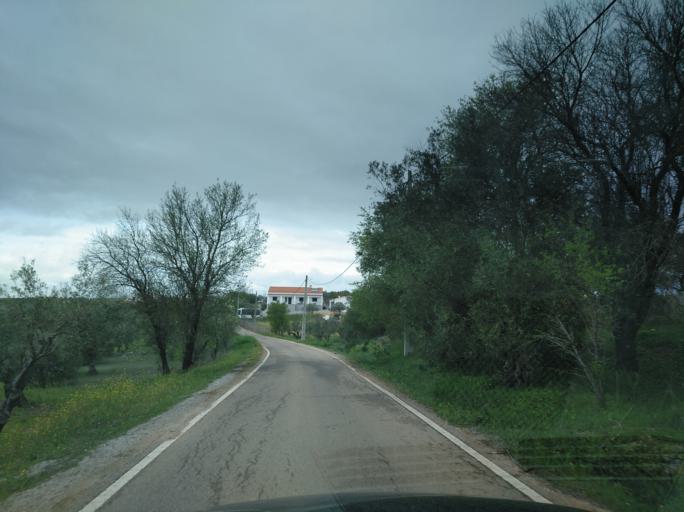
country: PT
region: Portalegre
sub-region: Campo Maior
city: Campo Maior
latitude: 38.9902
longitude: -7.0465
